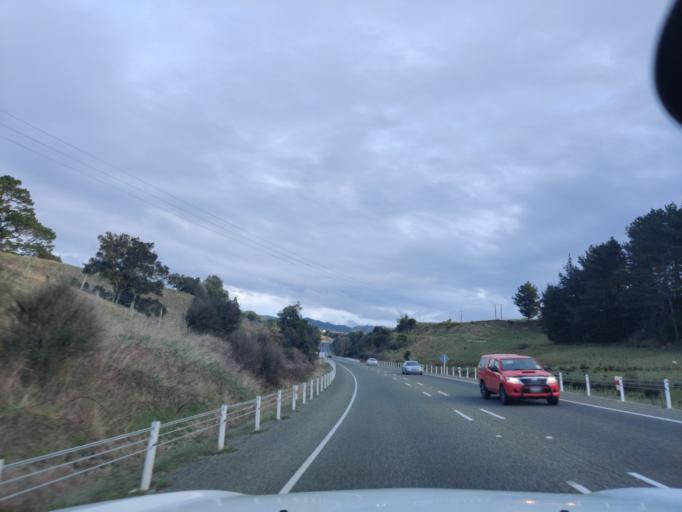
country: NZ
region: Manawatu-Wanganui
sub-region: Horowhenua District
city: Levin
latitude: -40.5676
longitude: 175.3915
